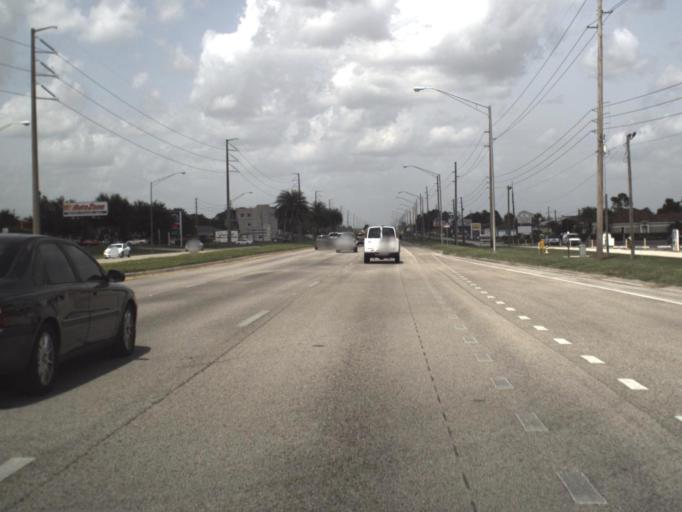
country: US
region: Florida
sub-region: Highlands County
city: Sebring
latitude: 27.5167
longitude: -81.4956
